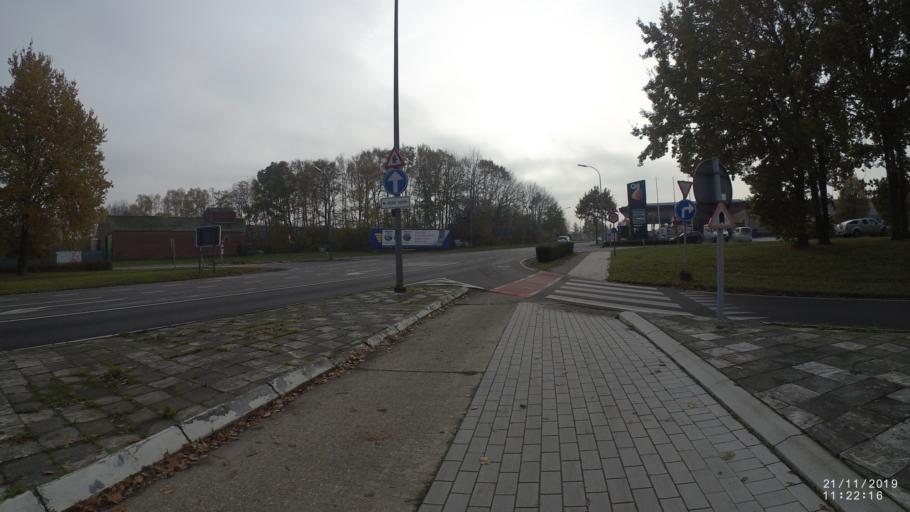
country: BE
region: Flanders
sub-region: Provincie Limburg
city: Sint-Truiden
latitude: 50.8188
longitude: 5.2071
